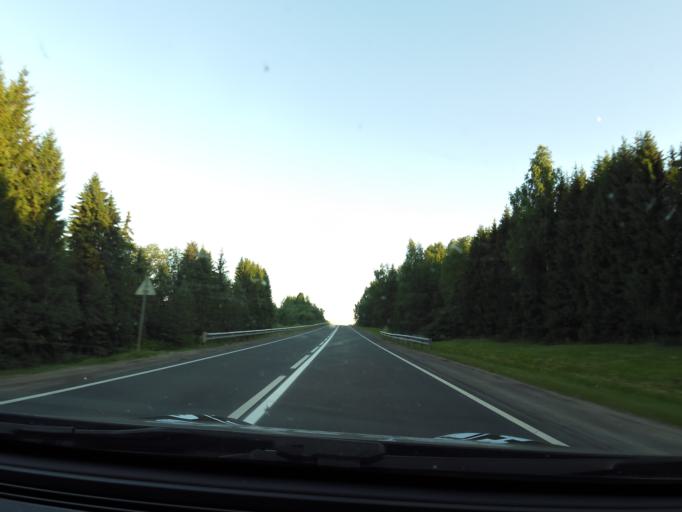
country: RU
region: Jaroslavl
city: Prechistoye
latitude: 58.4754
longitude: 40.3220
